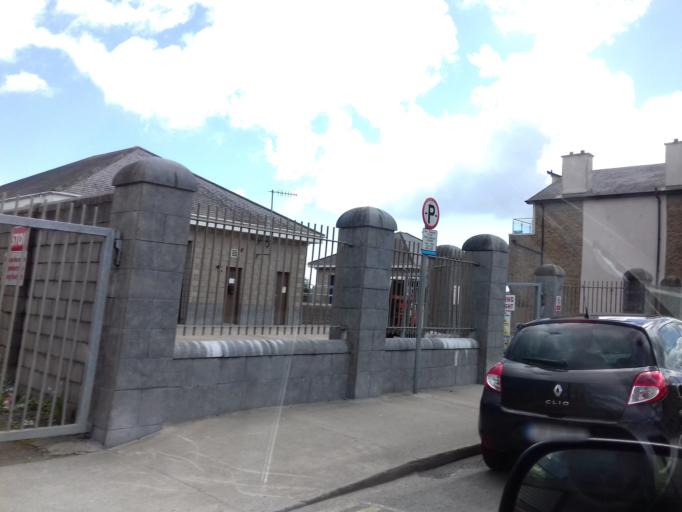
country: IE
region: Leinster
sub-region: Loch Garman
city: Loch Garman
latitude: 52.3349
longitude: -6.4560
